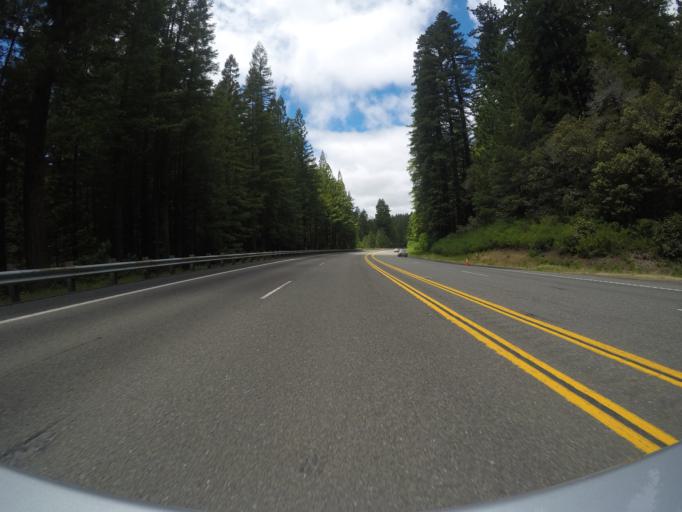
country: US
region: California
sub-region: Humboldt County
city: Redway
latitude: 40.2793
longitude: -123.8862
